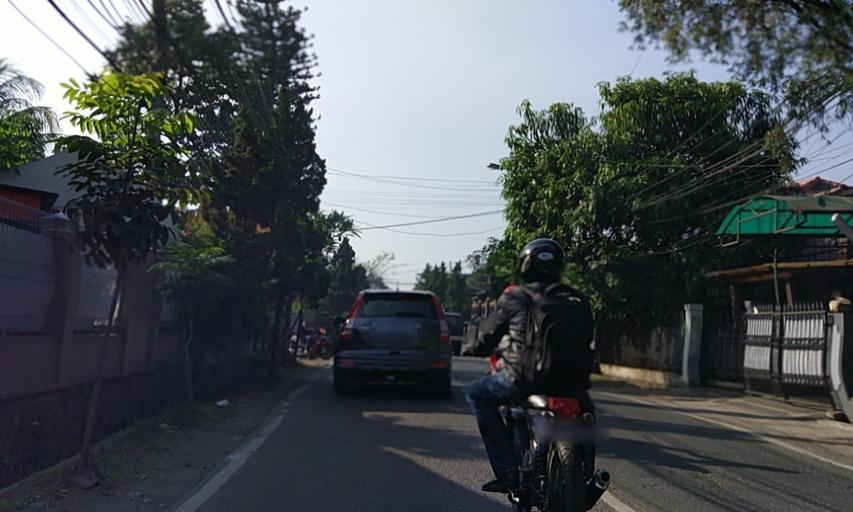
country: ID
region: West Java
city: Bandung
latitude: -6.9170
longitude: 107.6707
